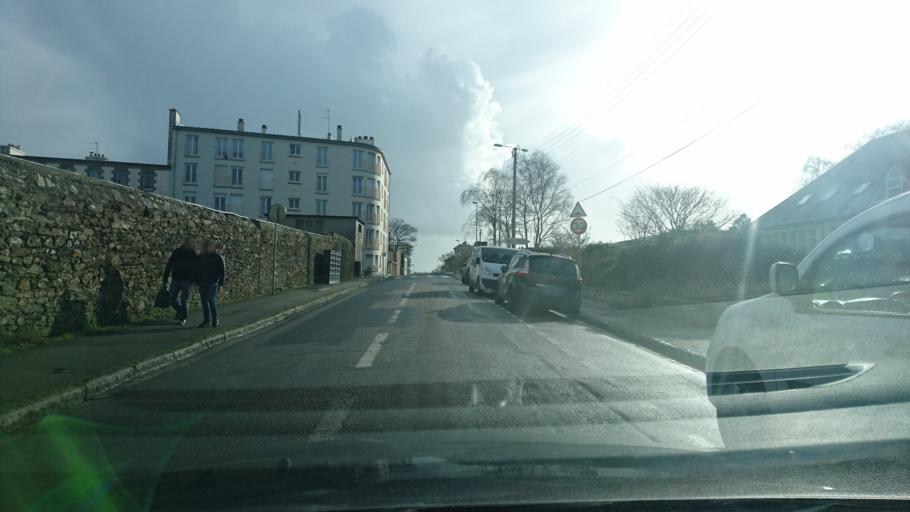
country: FR
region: Brittany
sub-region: Departement du Finistere
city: Brest
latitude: 48.3875
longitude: -4.5033
